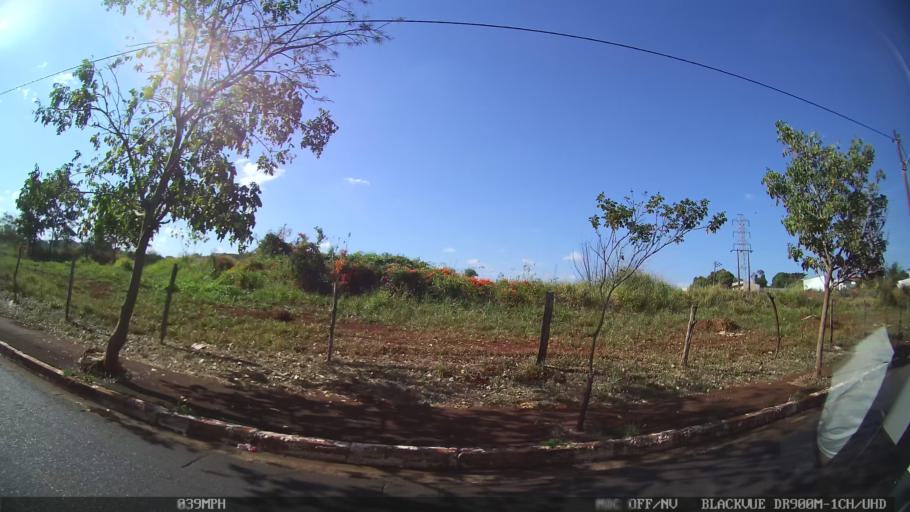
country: BR
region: Sao Paulo
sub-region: Ribeirao Preto
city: Ribeirao Preto
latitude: -21.1762
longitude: -47.7788
